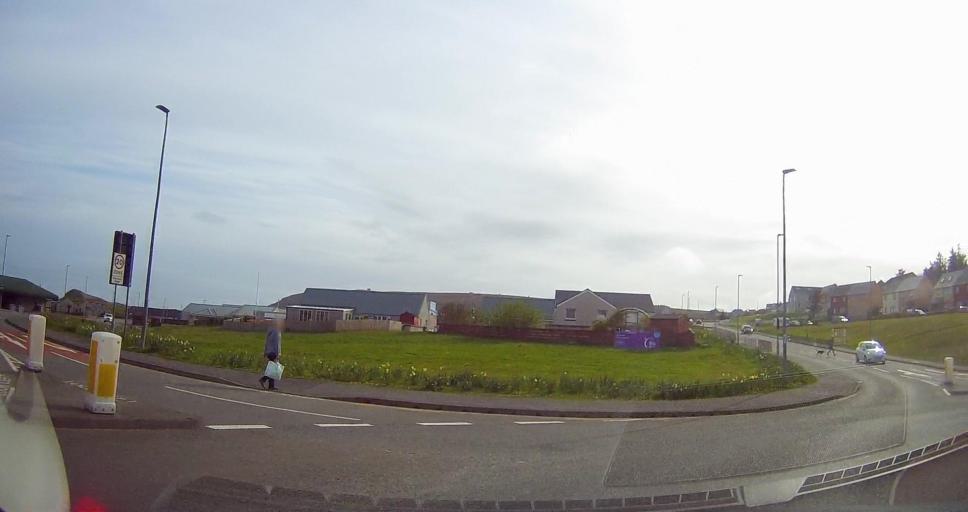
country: GB
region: Scotland
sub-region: Shetland Islands
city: Lerwick
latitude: 60.1455
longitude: -1.1700
